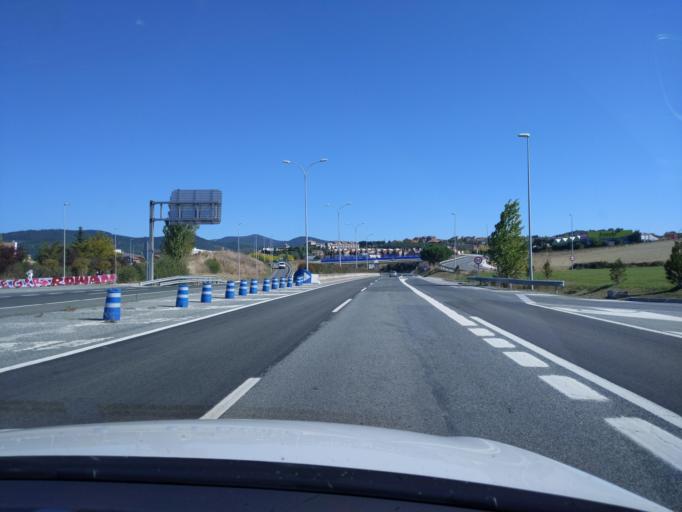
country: ES
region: Navarre
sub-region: Provincia de Navarra
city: Egues-Uharte
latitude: 42.8176
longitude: -1.5900
